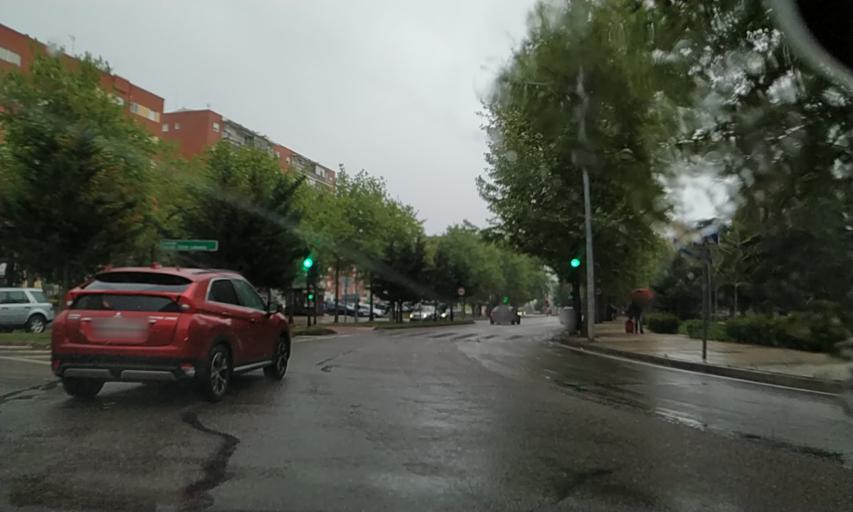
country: ES
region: Extremadura
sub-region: Provincia de Badajoz
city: Badajoz
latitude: 38.8691
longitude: -6.9732
